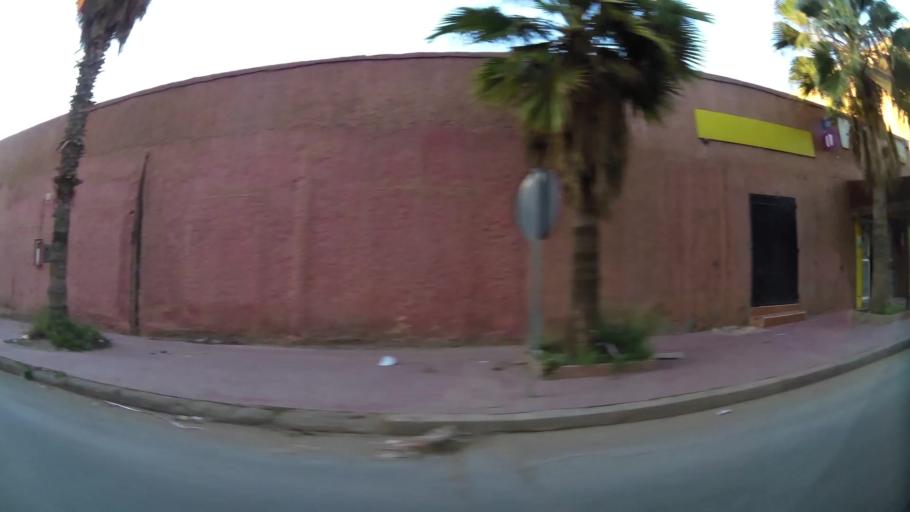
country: MA
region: Oriental
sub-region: Berkane-Taourirt
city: Berkane
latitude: 34.9184
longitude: -2.3269
